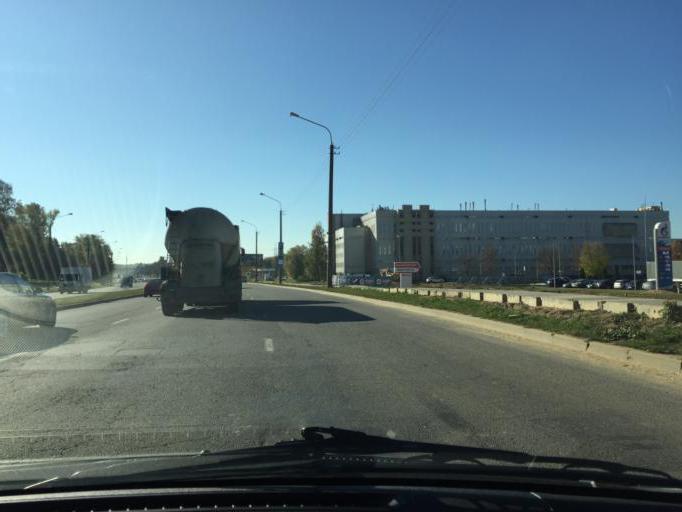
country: BY
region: Minsk
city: Syenitsa
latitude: 53.8419
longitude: 27.5334
